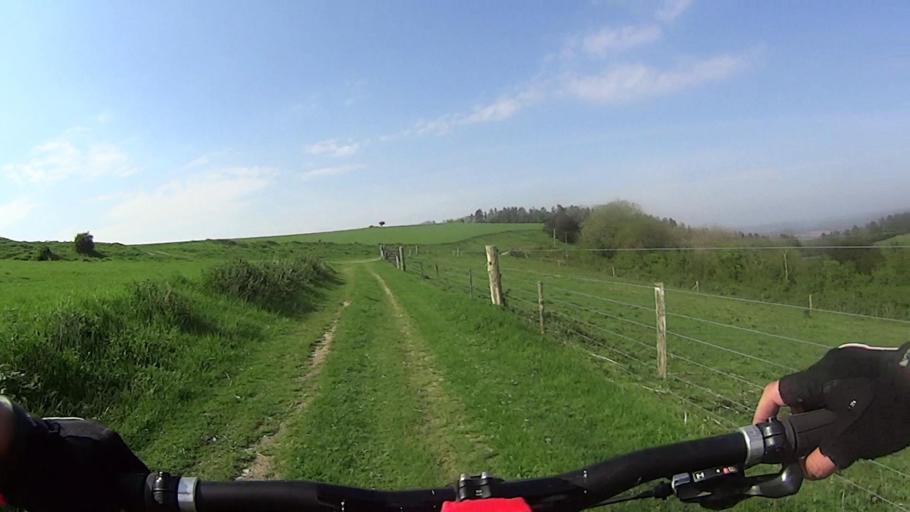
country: GB
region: England
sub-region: West Sussex
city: Milland
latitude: 50.9556
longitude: -0.8503
